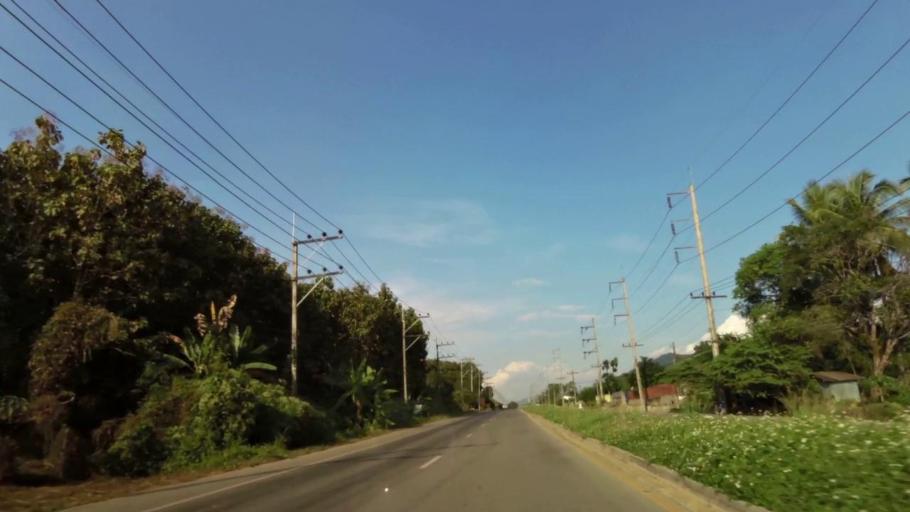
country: TH
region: Chiang Rai
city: Khun Tan
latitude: 19.8738
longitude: 100.2871
